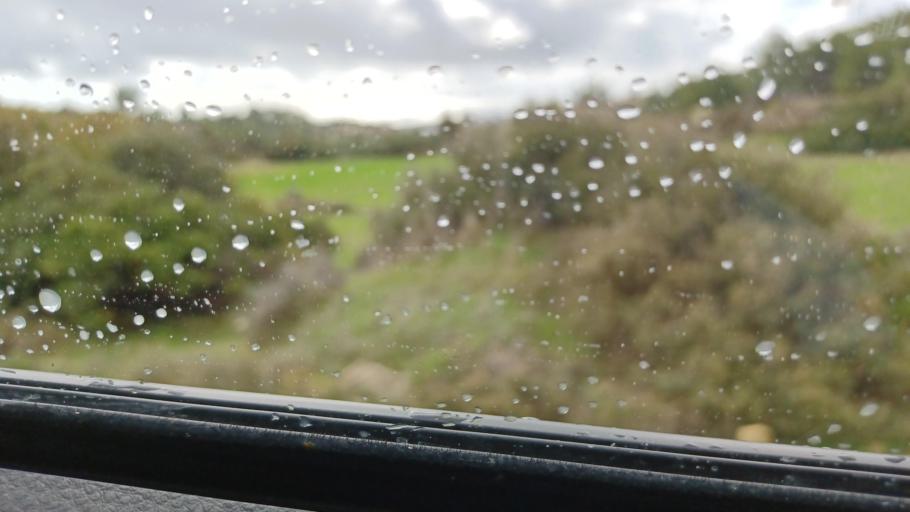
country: CY
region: Limassol
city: Sotira
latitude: 34.7447
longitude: 32.8429
